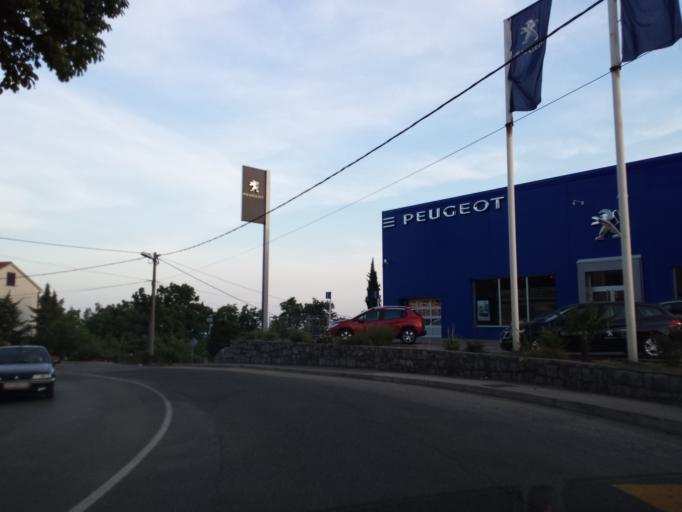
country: HR
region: Primorsko-Goranska
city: Rubesi
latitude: 45.3529
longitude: 14.3639
